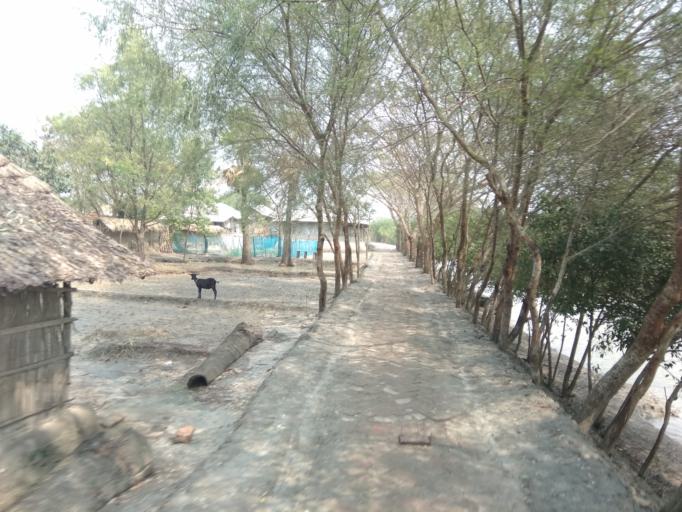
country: IN
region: West Bengal
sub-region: North 24 Parganas
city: Taki
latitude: 22.2582
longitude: 89.2582
